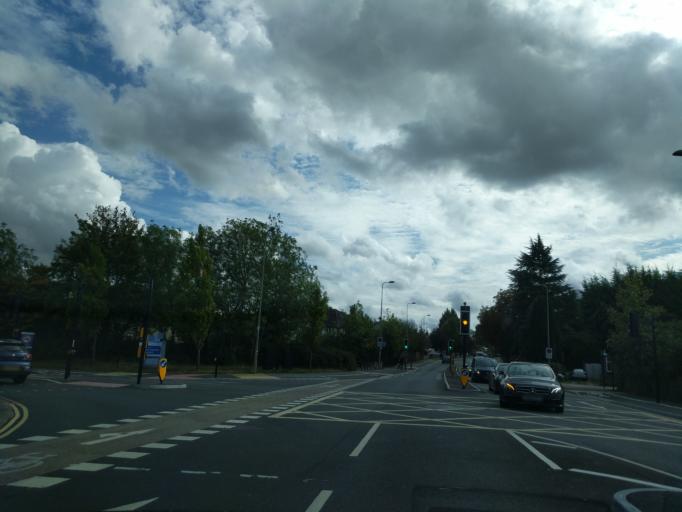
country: GB
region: England
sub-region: Oxfordshire
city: Oxford
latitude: 51.7638
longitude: -1.2256
